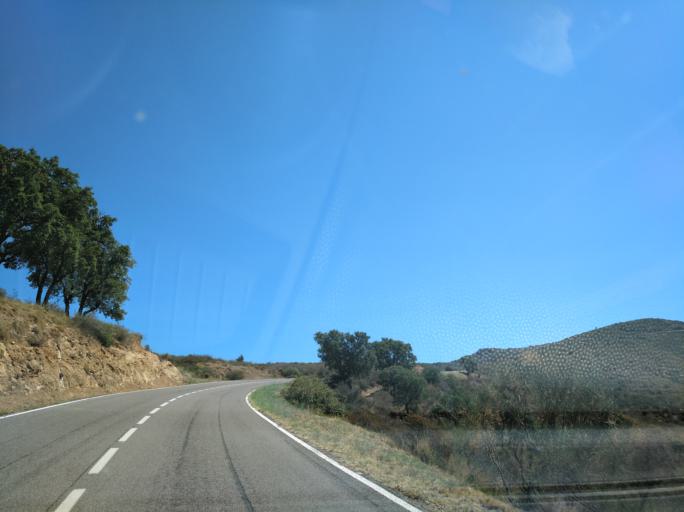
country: ES
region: Catalonia
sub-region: Provincia de Girona
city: Pau
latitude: 42.3370
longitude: 3.1207
